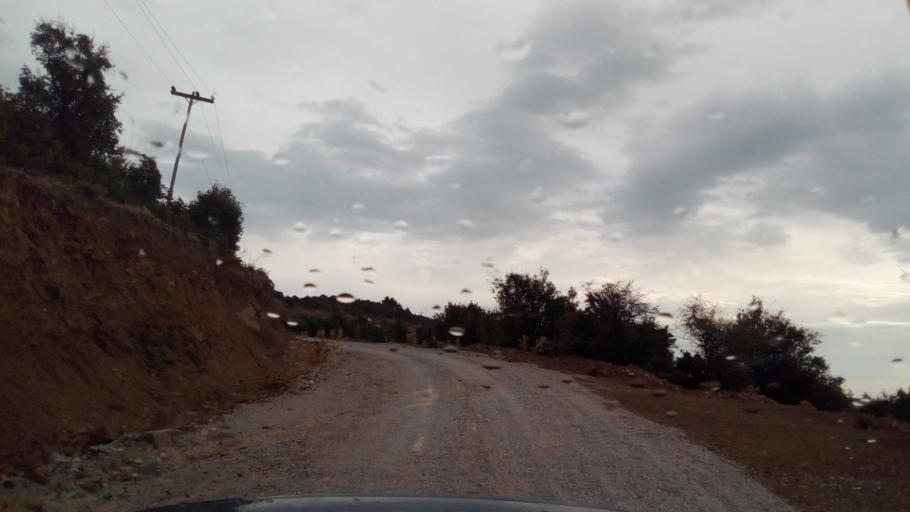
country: GR
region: West Greece
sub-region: Nomos Achaias
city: Kamarai
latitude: 38.4392
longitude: 22.0617
